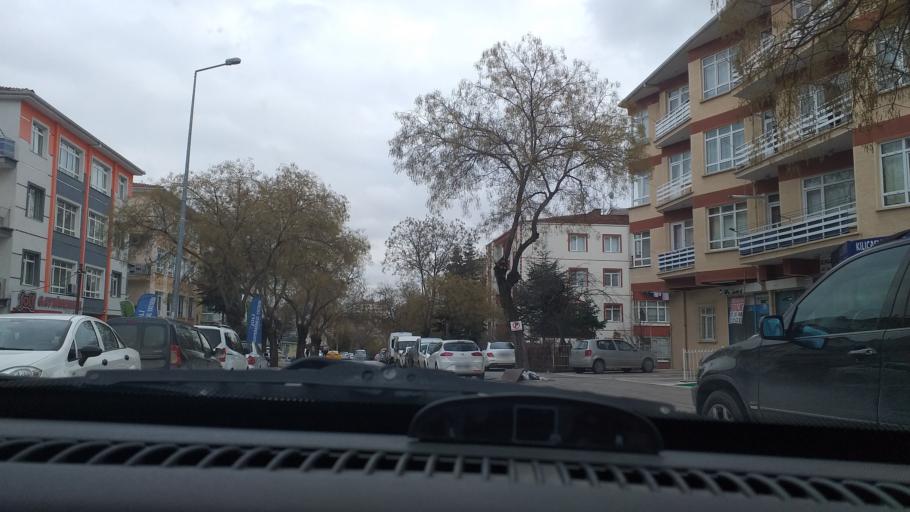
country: TR
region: Ankara
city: Ankara
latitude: 39.9800
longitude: 32.8304
